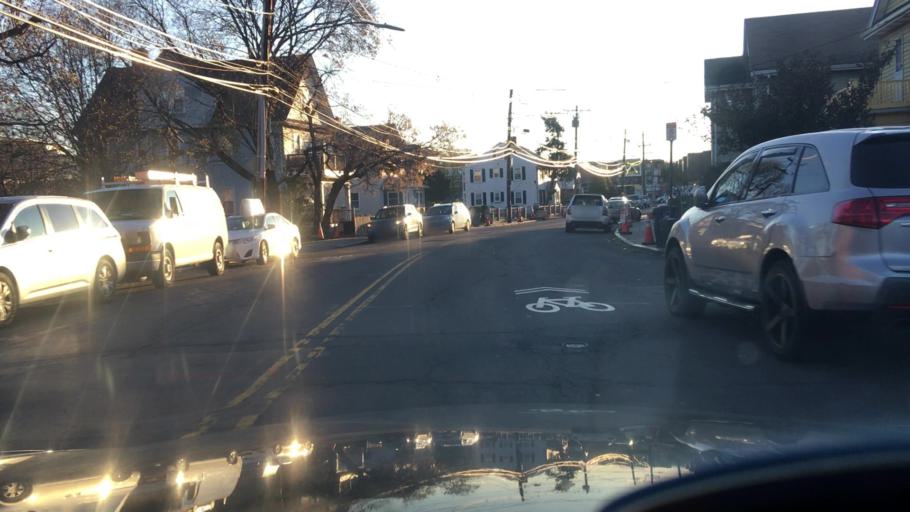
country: US
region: Massachusetts
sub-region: Middlesex County
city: Watertown
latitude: 42.3555
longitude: -71.1520
